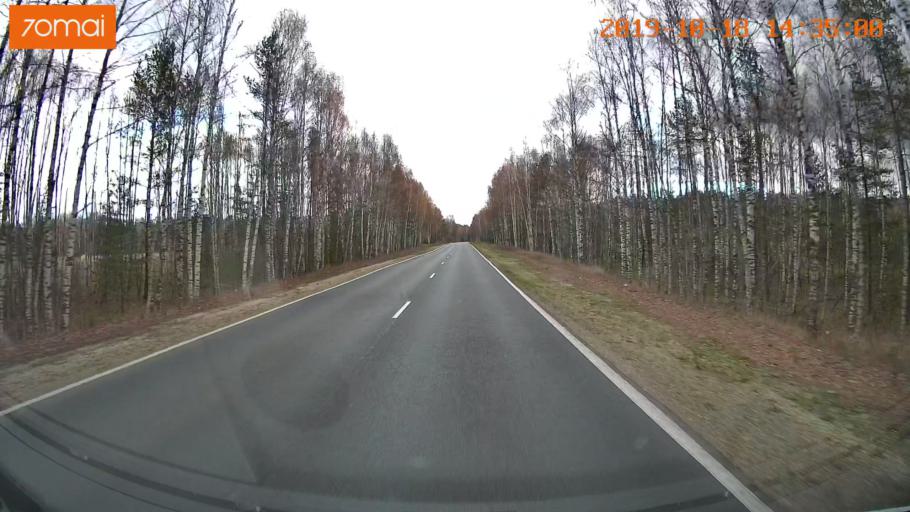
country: RU
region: Vladimir
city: Velikodvorskiy
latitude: 55.2184
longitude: 40.6275
